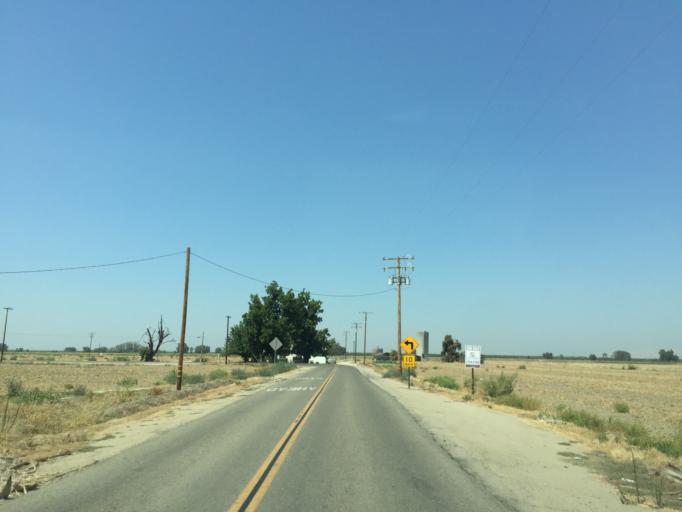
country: US
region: California
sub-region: Tulare County
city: Visalia
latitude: 36.3642
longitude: -119.3144
